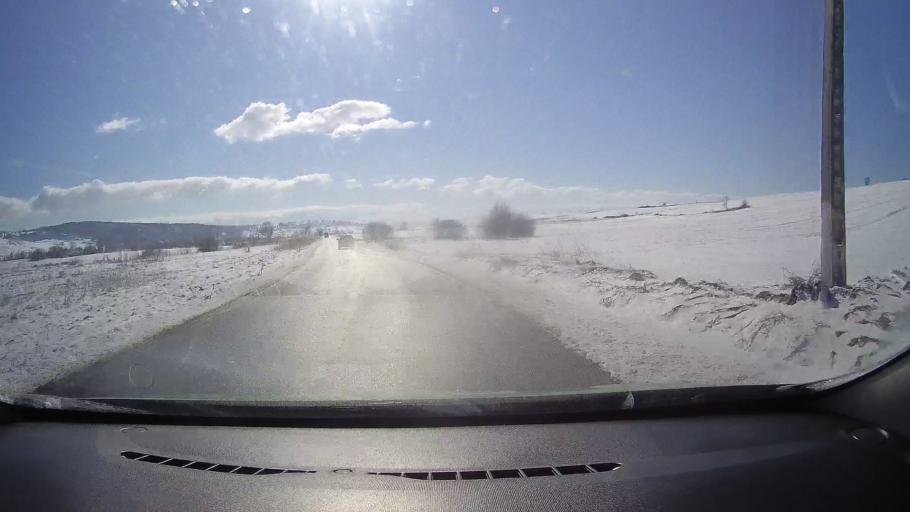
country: RO
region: Sibiu
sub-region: Comuna Vurpar
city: Vurpar
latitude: 45.8727
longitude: 24.3180
